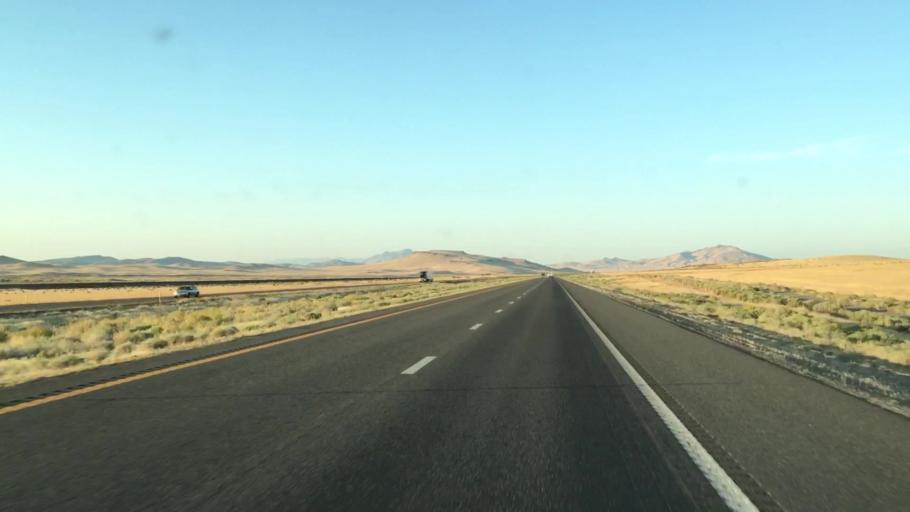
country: US
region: Nevada
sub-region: Humboldt County
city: Winnemucca
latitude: 40.8642
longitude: -117.9461
